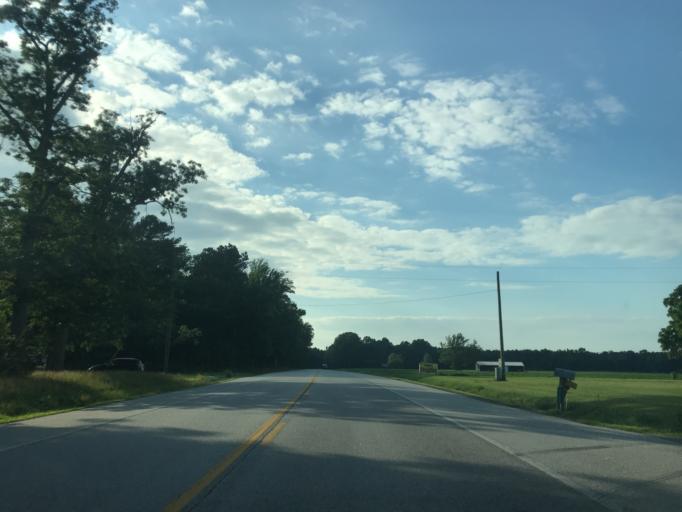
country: US
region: Maryland
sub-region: Caroline County
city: Federalsburg
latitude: 38.7313
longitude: -75.7877
